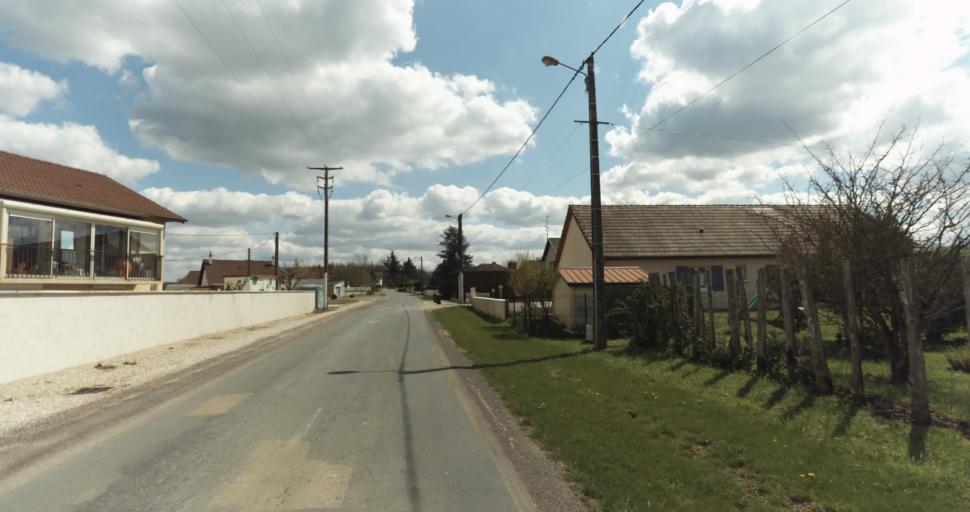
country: FR
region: Bourgogne
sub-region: Departement de la Cote-d'Or
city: Auxonne
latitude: 47.1869
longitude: 5.4046
